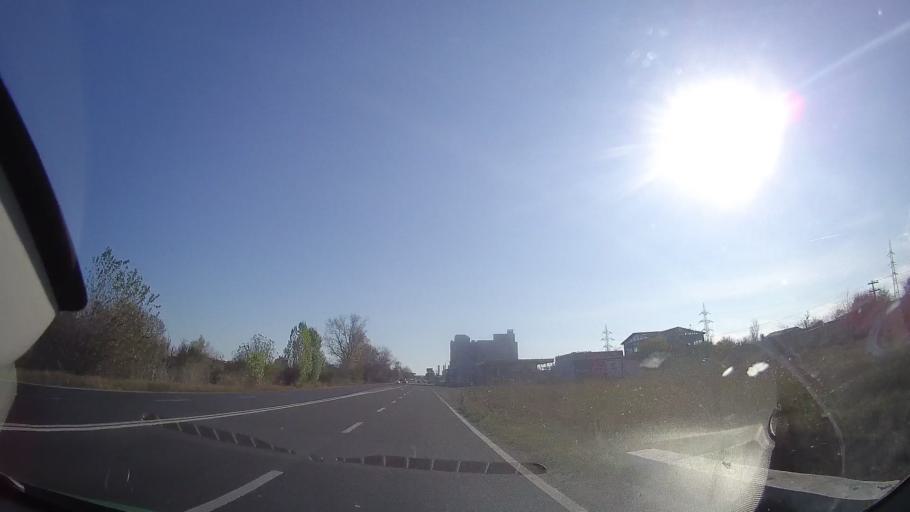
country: RO
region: Constanta
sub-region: Municipiul Mangalia
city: Mangalia
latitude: 43.8331
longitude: 28.5782
